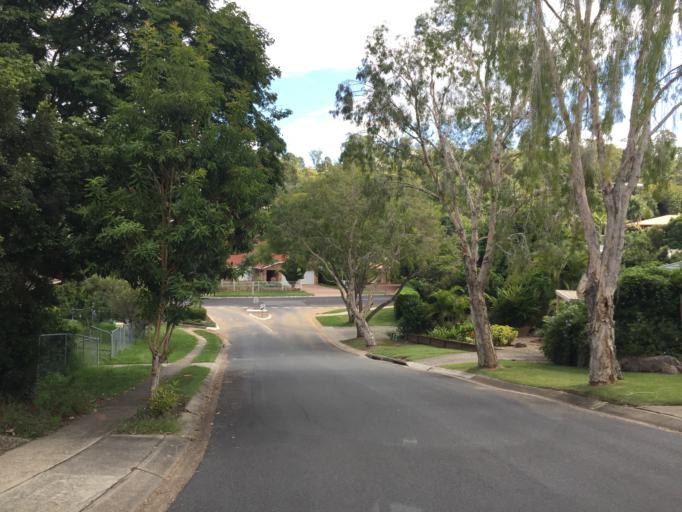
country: AU
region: Queensland
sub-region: Moreton Bay
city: Ferny Hills
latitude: -27.4340
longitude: 152.9360
